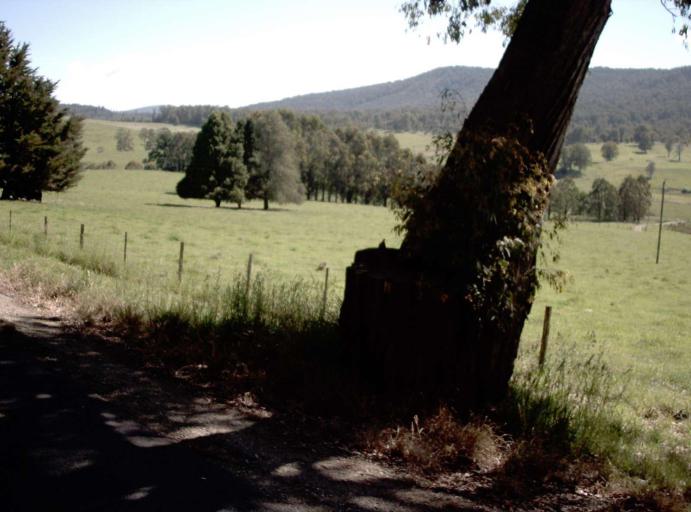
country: AU
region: New South Wales
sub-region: Bombala
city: Bombala
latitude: -37.1772
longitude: 148.7251
